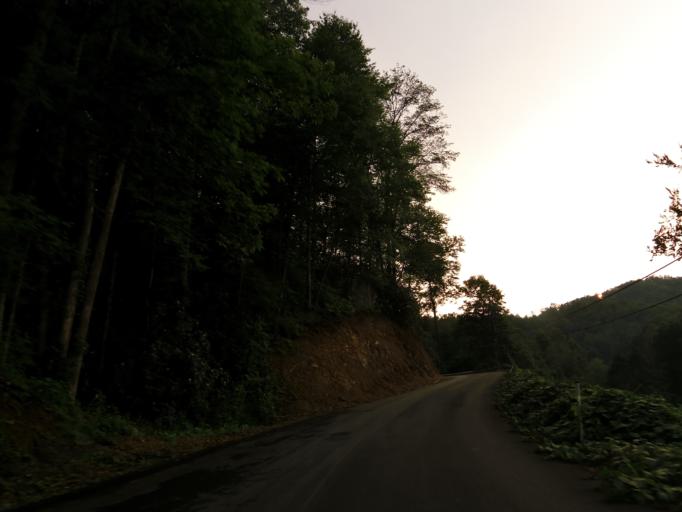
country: US
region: Tennessee
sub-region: Sevier County
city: Seymour
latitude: 35.7546
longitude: -83.7238
